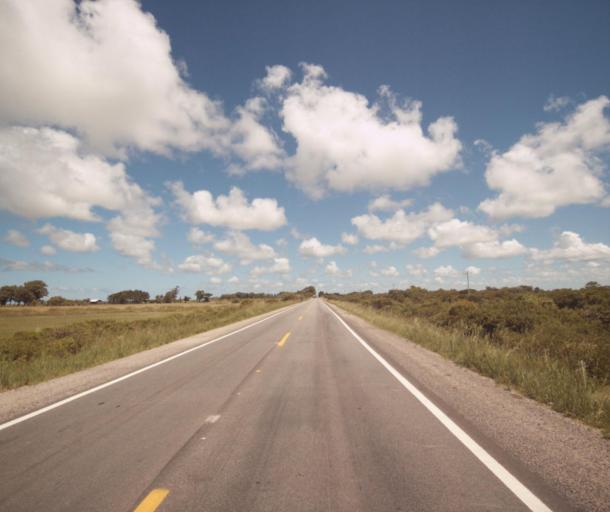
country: UY
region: Cerro Largo
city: Rio Branco
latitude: -32.9903
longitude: -52.8142
